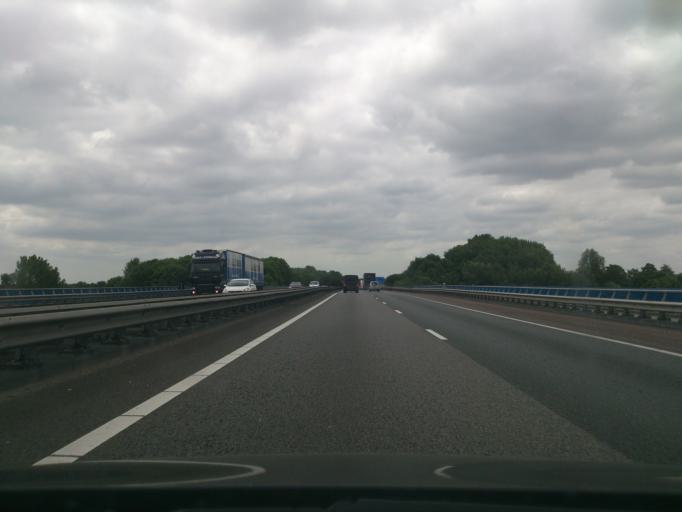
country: NL
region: North Brabant
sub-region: Gemeente Landerd
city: Reek
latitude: 51.7950
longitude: 5.6642
